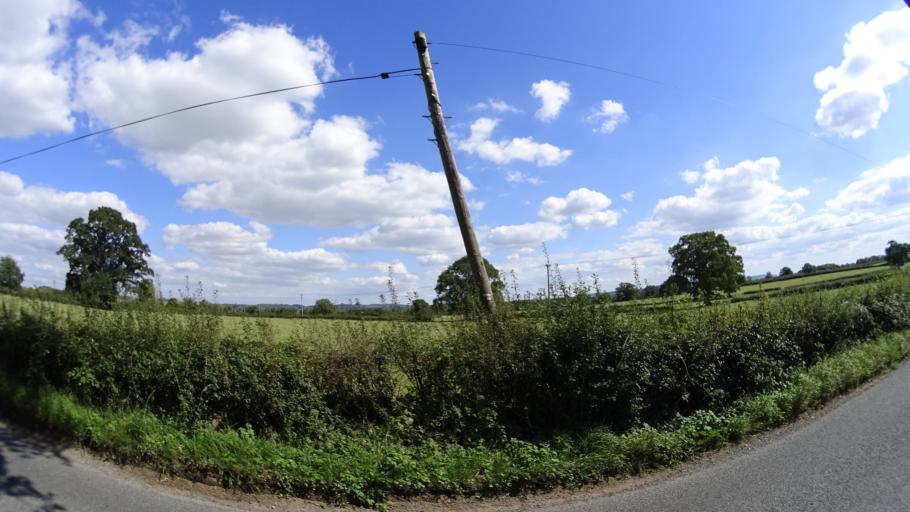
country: GB
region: England
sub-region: Wiltshire
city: Mere
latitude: 51.0849
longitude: -2.2812
